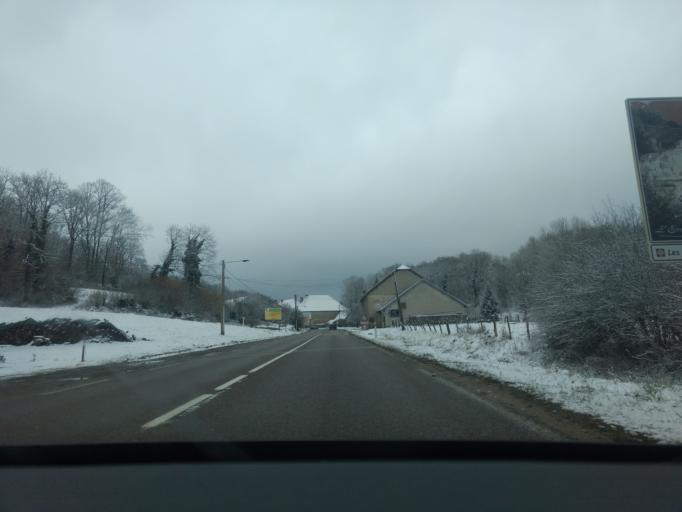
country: FR
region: Franche-Comte
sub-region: Departement du Jura
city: Champagnole
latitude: 46.8019
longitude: 5.8314
